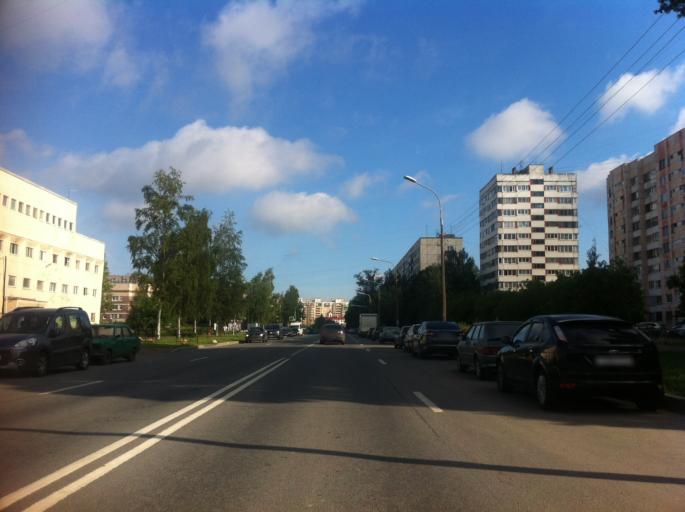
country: RU
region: St.-Petersburg
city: Dachnoye
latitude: 59.8359
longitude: 30.2166
